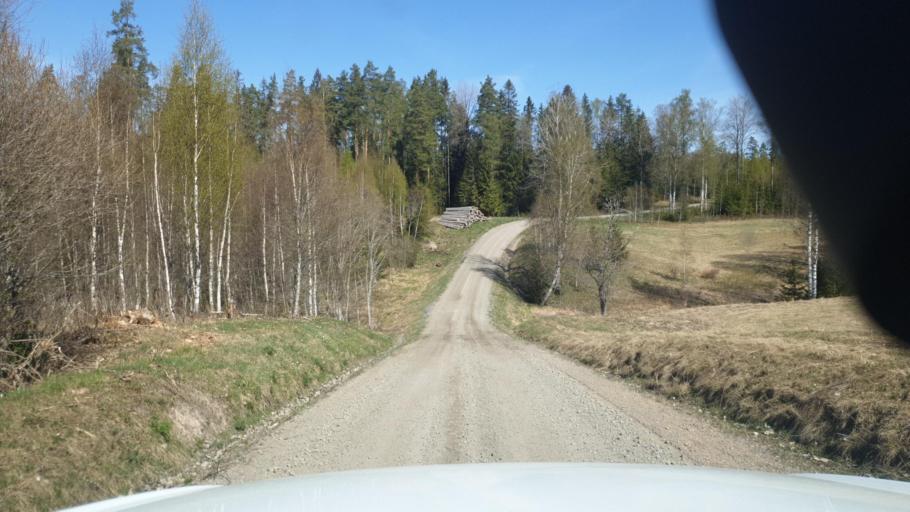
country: SE
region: Vaermland
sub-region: Karlstads Kommun
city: Edsvalla
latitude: 59.4729
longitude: 13.1271
